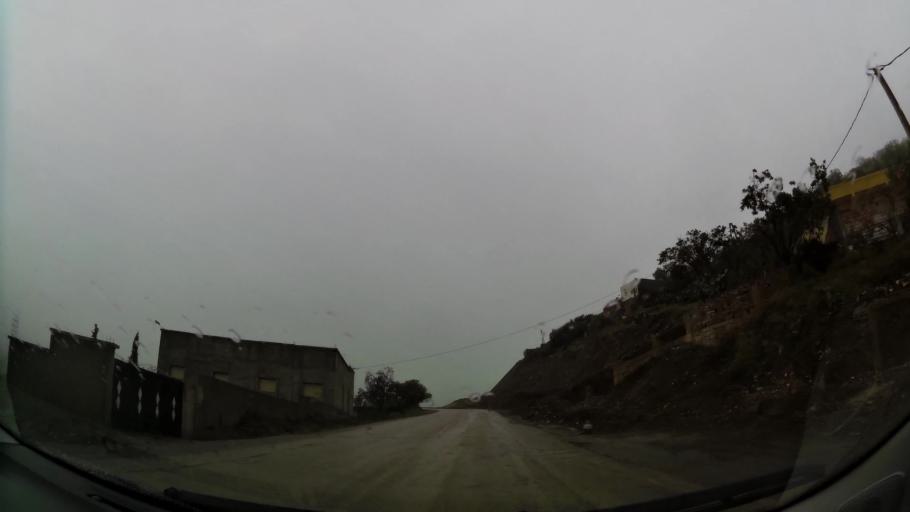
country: MA
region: Taza-Al Hoceima-Taounate
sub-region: Taza
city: Aknoul
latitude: 34.7823
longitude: -3.7712
